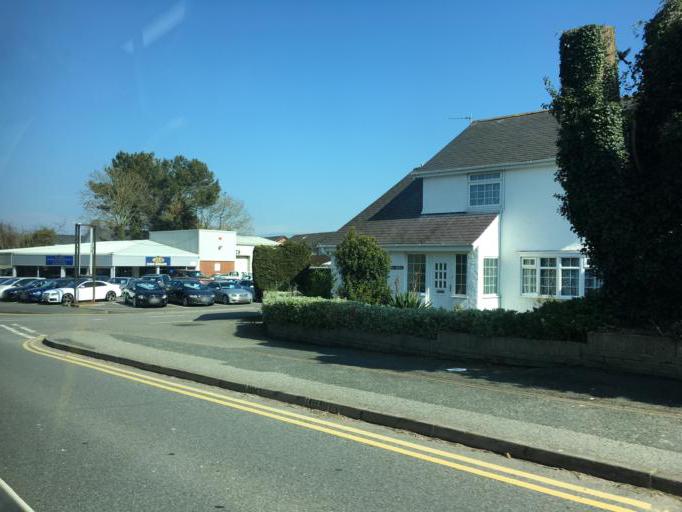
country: GB
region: Wales
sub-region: Anglesey
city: Menai Bridge
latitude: 53.2065
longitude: -4.1709
